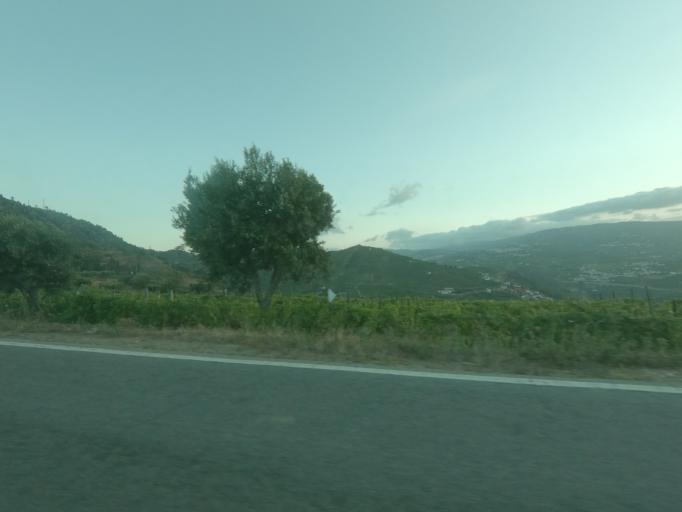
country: PT
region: Vila Real
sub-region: Peso da Regua
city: Peso da Regua
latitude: 41.1318
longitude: -7.7513
